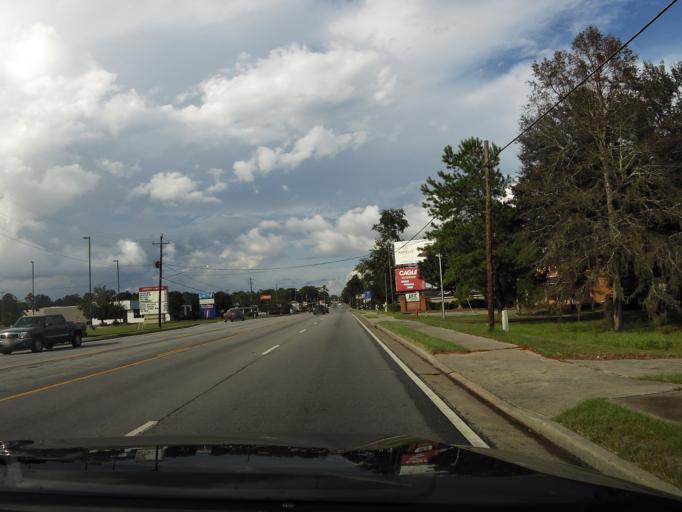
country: US
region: Georgia
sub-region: Liberty County
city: Hinesville
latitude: 31.8333
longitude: -81.5966
